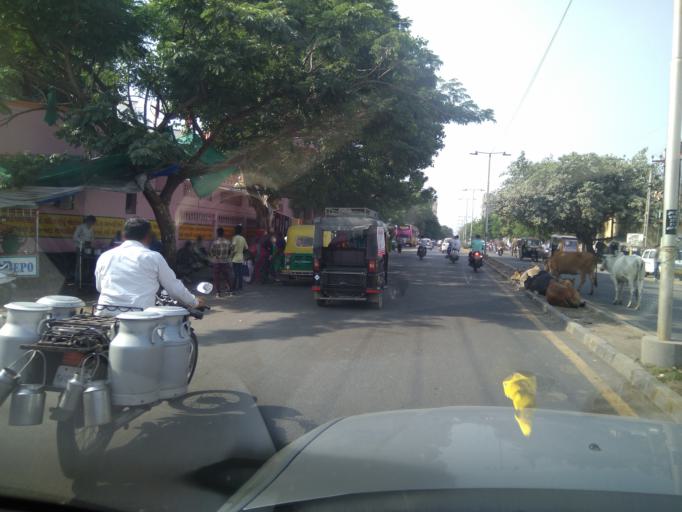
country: IN
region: Gujarat
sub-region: Jamnagar
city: Jamnagar
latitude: 22.4647
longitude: 70.0520
